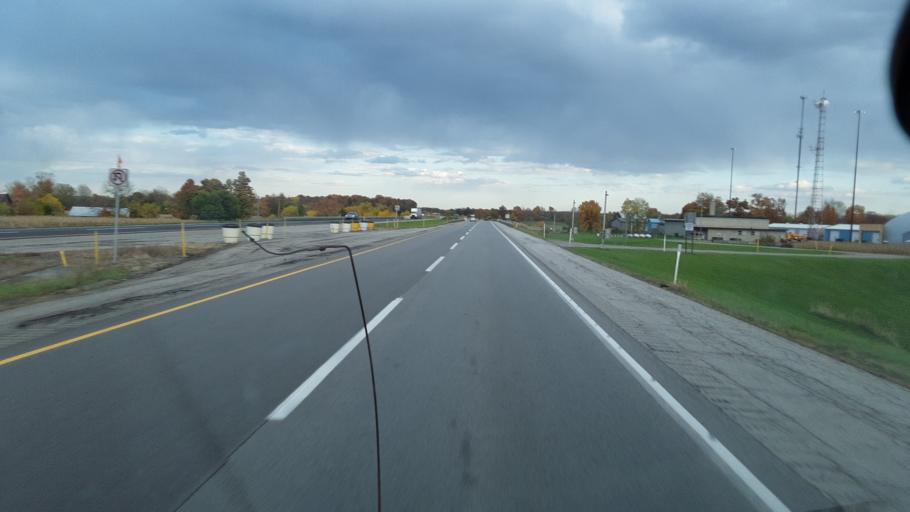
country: US
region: Michigan
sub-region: Branch County
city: Bronson
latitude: 41.7536
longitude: -85.1175
